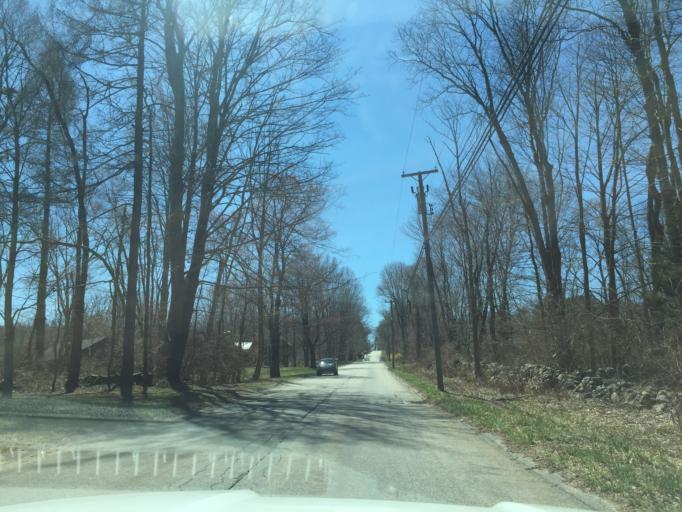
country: US
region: Connecticut
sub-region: Windham County
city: South Woodstock
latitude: 41.9564
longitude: -71.9727
